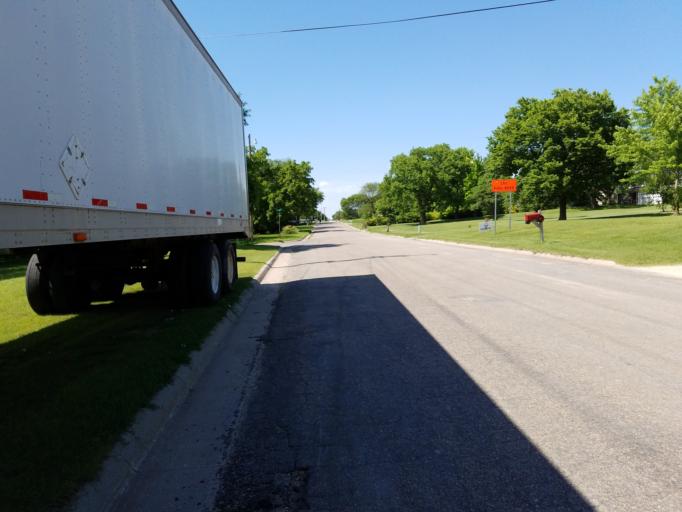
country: US
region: Kansas
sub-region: Jewell County
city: Mankato
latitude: 39.7854
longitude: -98.2036
